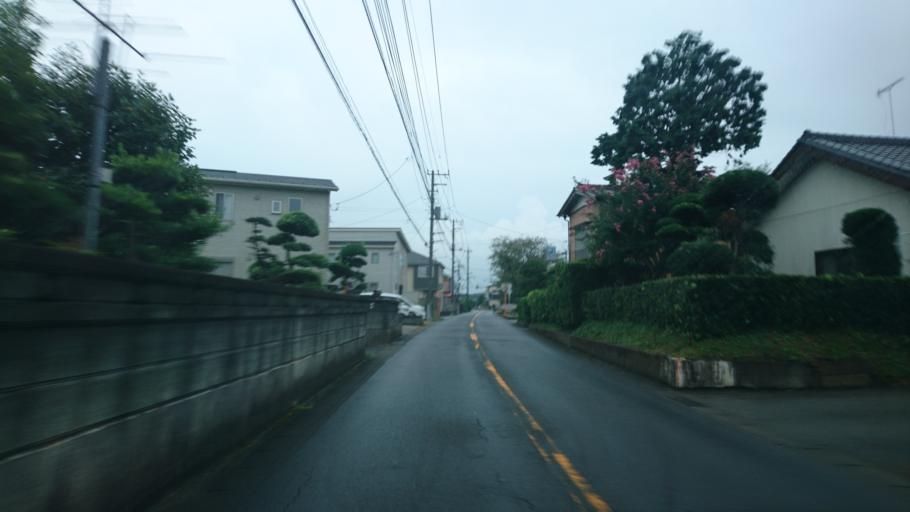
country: JP
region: Chiba
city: Kimitsu
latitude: 35.3288
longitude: 139.9300
